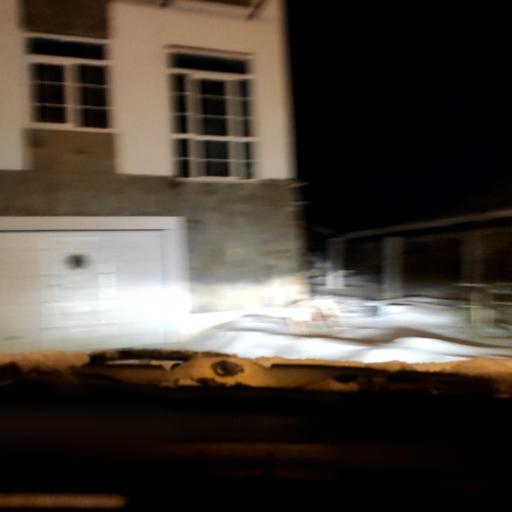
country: RU
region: Perm
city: Perm
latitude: 58.0352
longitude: 56.3942
